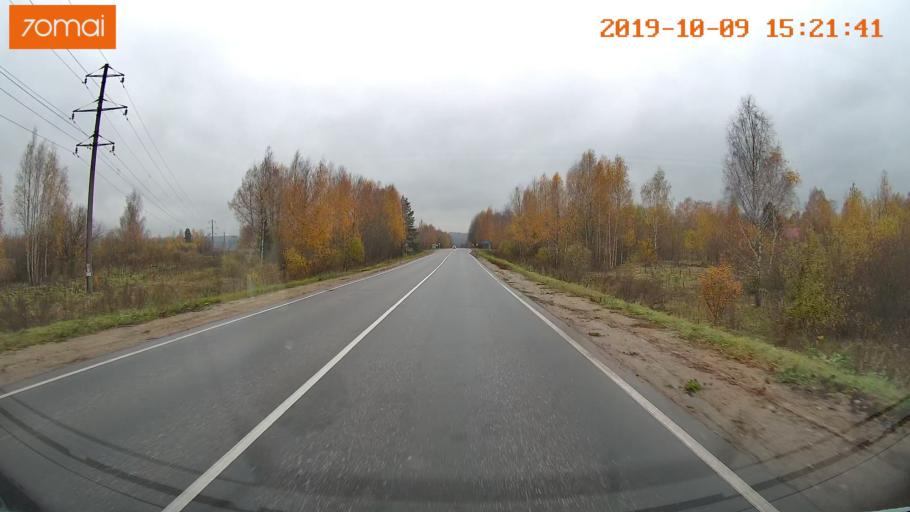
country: RU
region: Kostroma
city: Susanino
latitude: 58.0518
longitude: 41.5139
